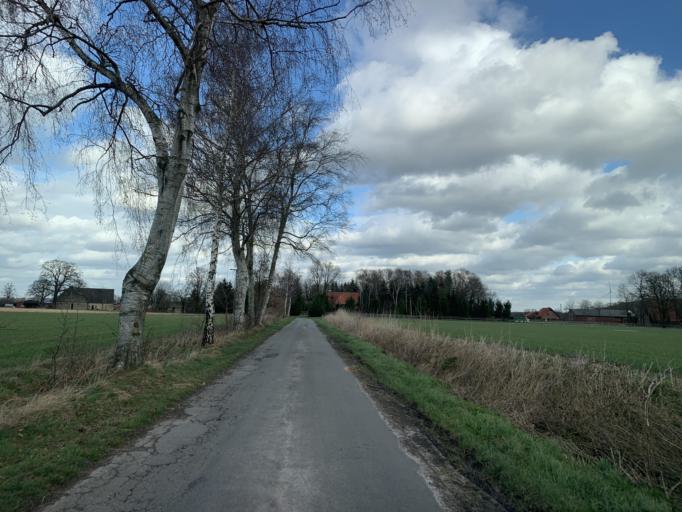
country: DE
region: North Rhine-Westphalia
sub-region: Regierungsbezirk Munster
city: Horstmar
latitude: 52.1028
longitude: 7.3092
